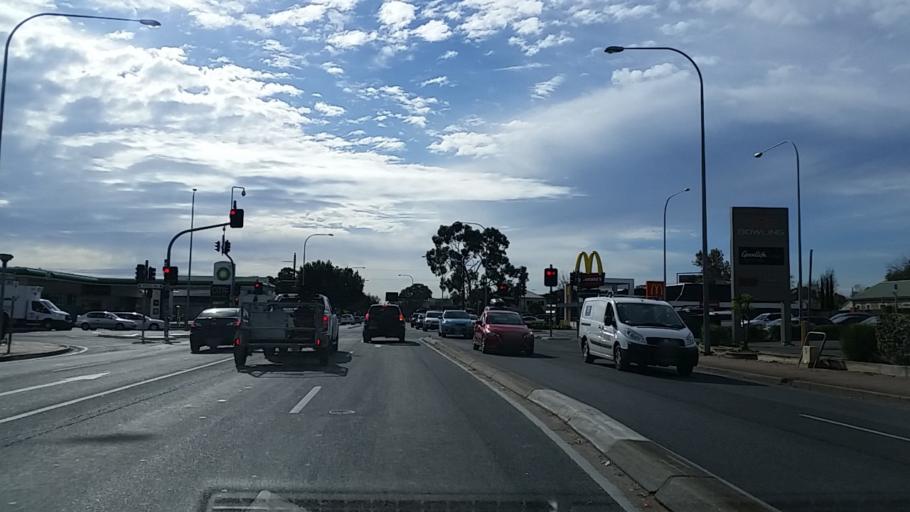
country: AU
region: South Australia
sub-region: Unley
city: Millswood
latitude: -34.9669
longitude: 138.5908
